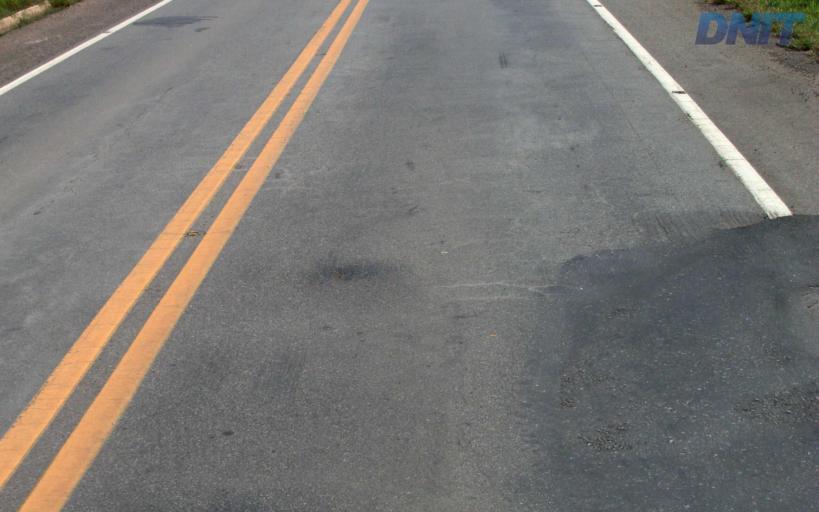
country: BR
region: Minas Gerais
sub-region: Belo Oriente
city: Belo Oriente
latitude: -19.0996
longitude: -42.1981
